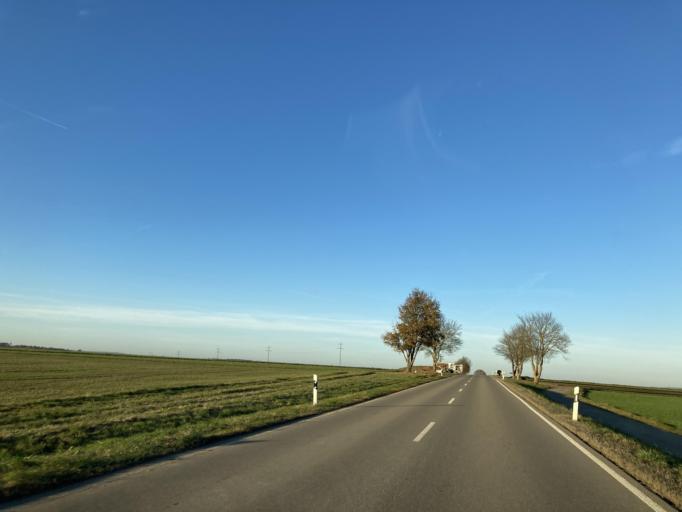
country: DE
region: Baden-Wuerttemberg
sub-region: Tuebingen Region
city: Hirrlingen
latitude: 48.4379
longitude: 8.8778
